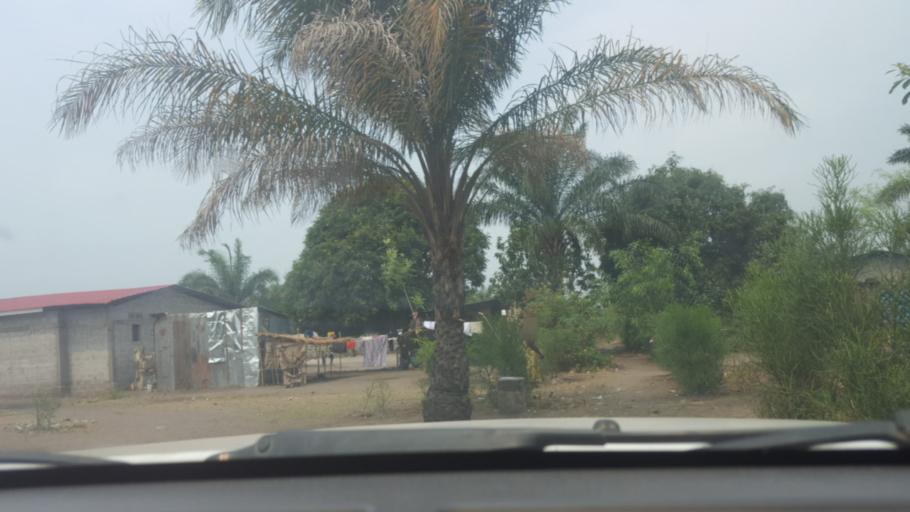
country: CD
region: Kinshasa
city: Masina
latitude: -4.3606
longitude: 15.5124
